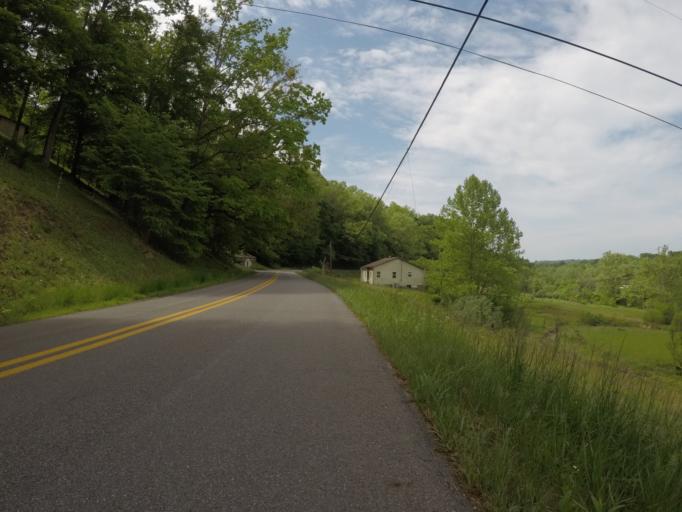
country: US
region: West Virginia
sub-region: Wayne County
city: Ceredo
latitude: 38.3450
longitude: -82.5680
